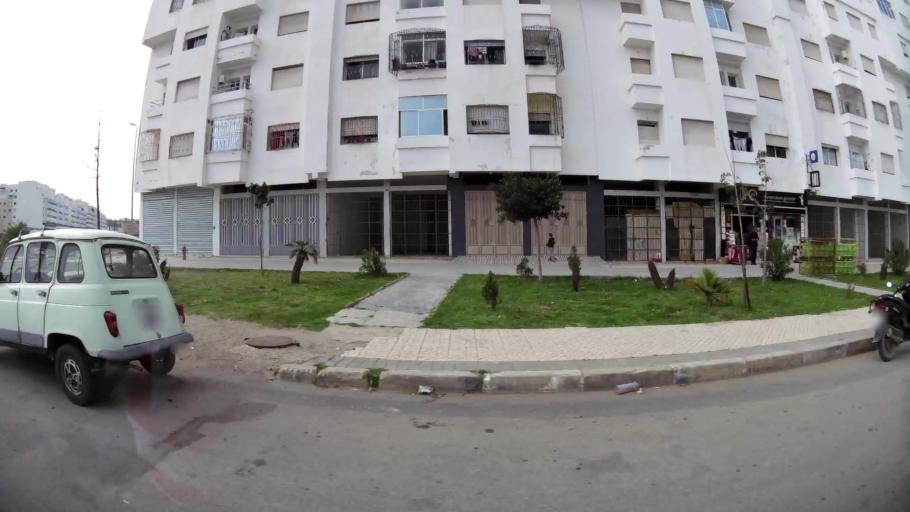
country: MA
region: Tanger-Tetouan
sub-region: Tanger-Assilah
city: Boukhalef
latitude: 35.7461
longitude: -5.8521
